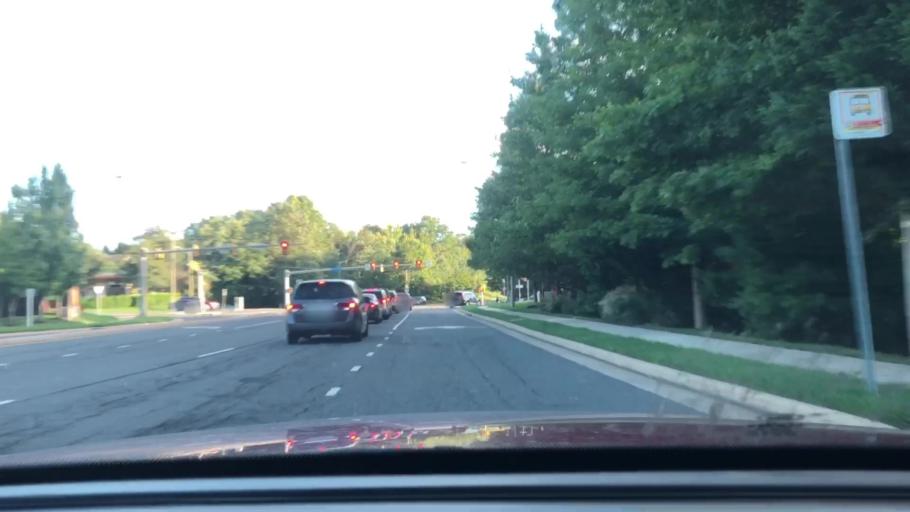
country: US
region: Virginia
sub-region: Fairfax County
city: Centreville
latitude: 38.8405
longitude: -77.4117
